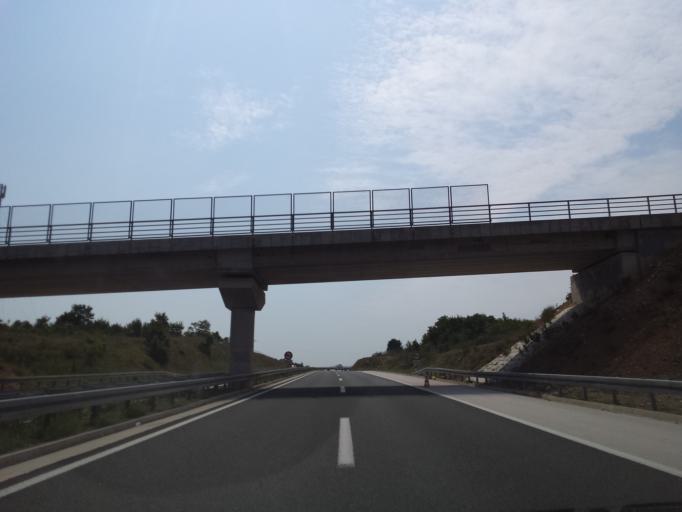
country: HR
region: Zadarska
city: Posedarje
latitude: 44.2072
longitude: 15.4451
